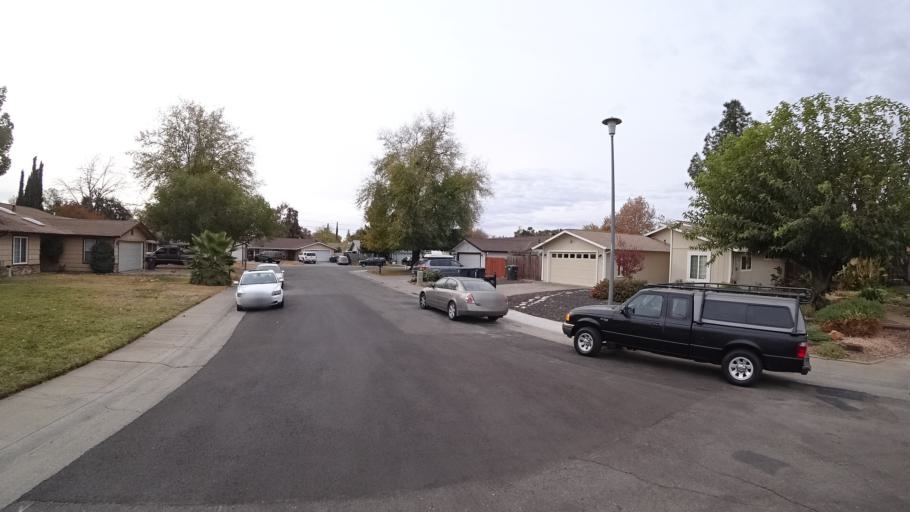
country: US
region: California
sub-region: Sacramento County
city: Citrus Heights
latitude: 38.7155
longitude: -121.2958
